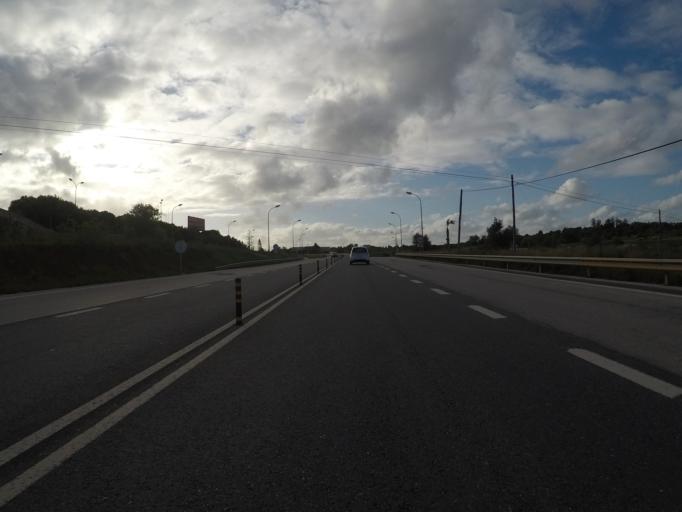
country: PT
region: Faro
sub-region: Portimao
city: Portimao
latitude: 37.1601
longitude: -8.5551
